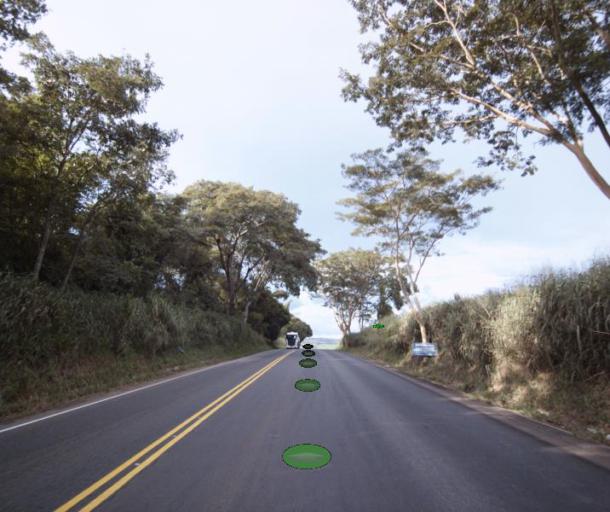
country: BR
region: Goias
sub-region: Ceres
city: Ceres
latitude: -15.1456
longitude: -49.5315
